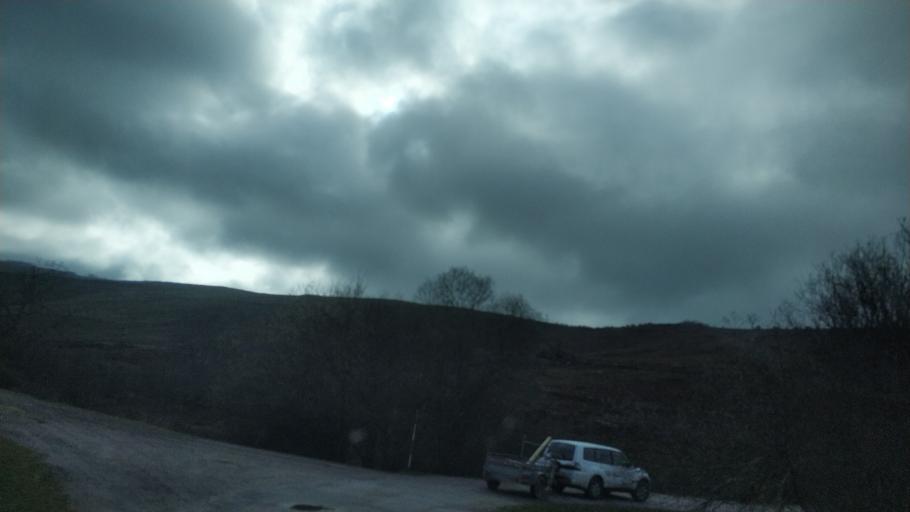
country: ES
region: Castille and Leon
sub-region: Provincia de Burgos
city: Arija
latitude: 42.9130
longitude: -3.9943
